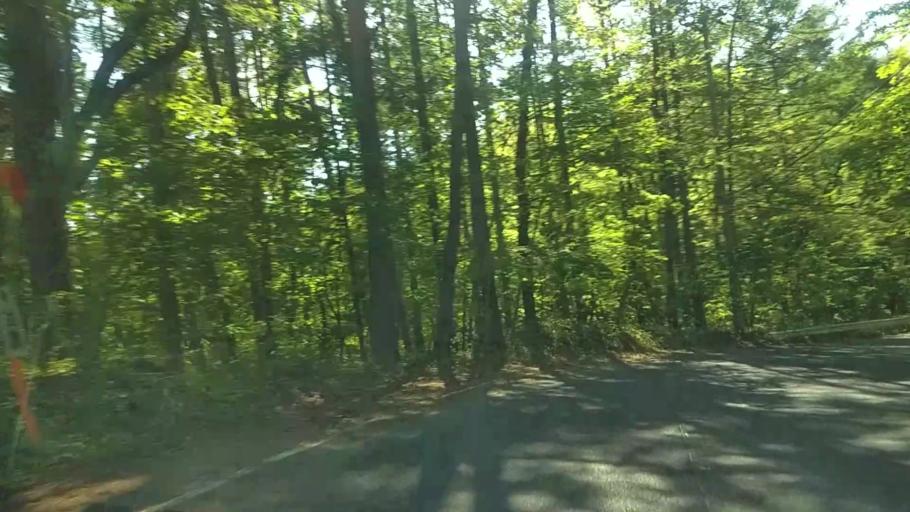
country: JP
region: Yamanashi
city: Nirasaki
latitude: 35.8930
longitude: 138.4033
